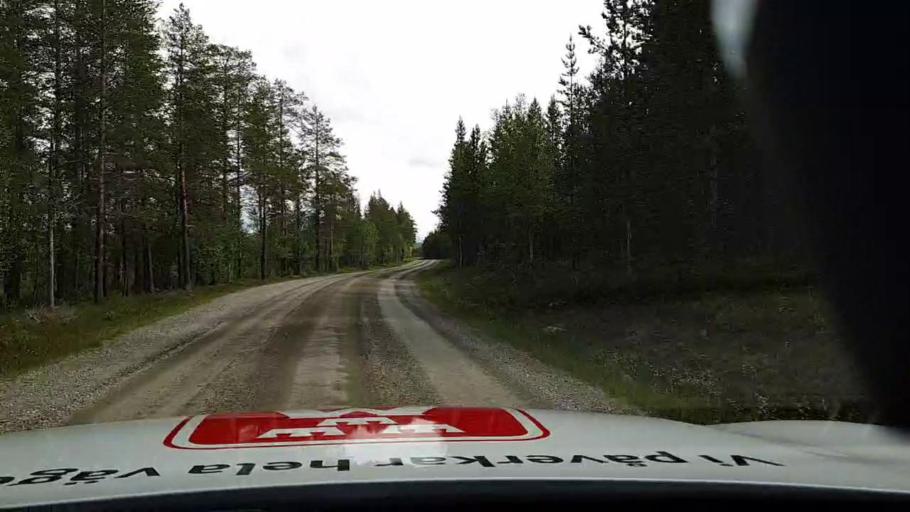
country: SE
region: Jaemtland
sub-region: Are Kommun
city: Jarpen
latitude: 62.4963
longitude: 13.5025
